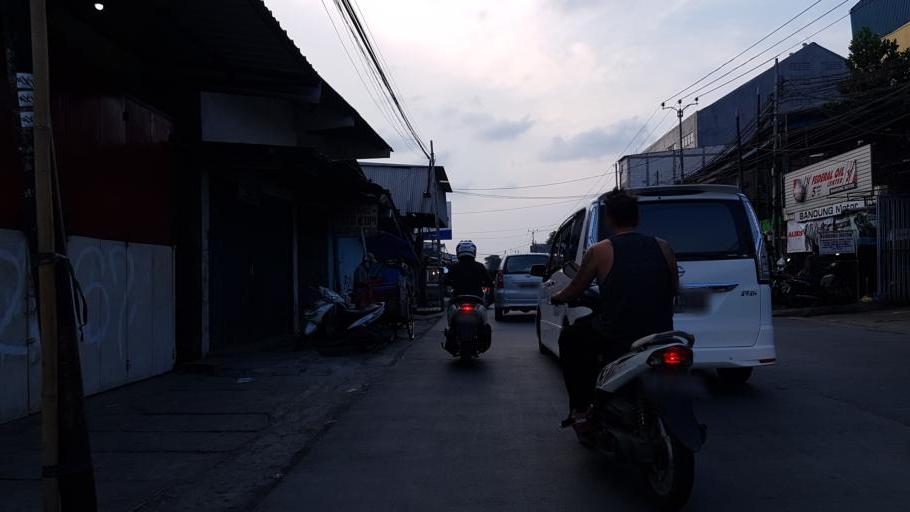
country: ID
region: Jakarta Raya
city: Jakarta
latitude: -6.1379
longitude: 106.7598
